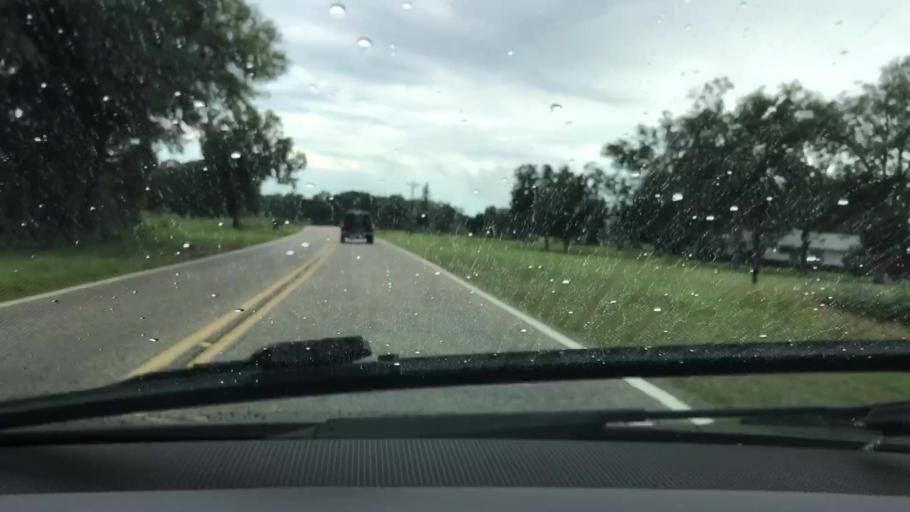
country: US
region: Alabama
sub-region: Geneva County
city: Samson
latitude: 31.1214
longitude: -86.1246
